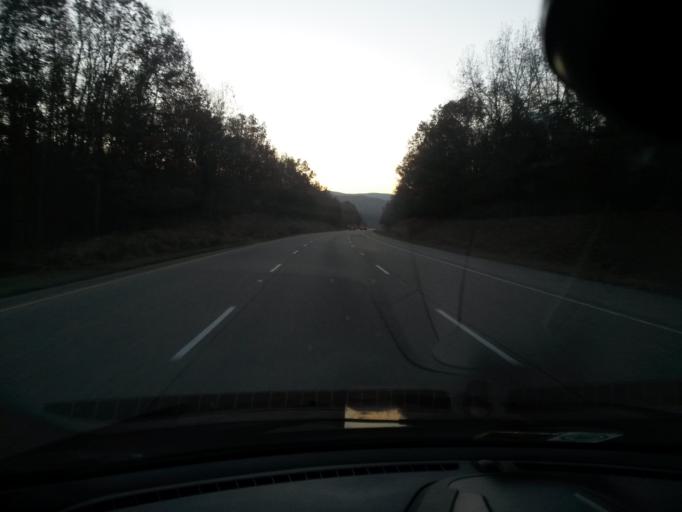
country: US
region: Virginia
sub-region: Alleghany County
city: Clifton Forge
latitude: 37.8287
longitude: -79.7540
